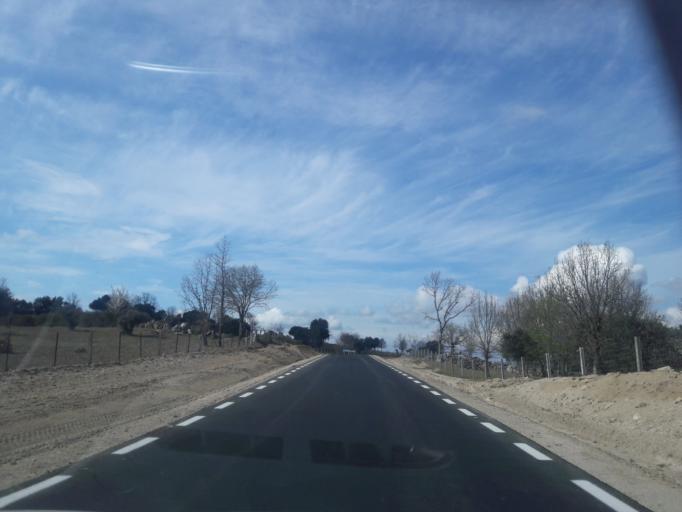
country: ES
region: Castille and Leon
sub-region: Provincia de Salamanca
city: Monleon
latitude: 40.5369
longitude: -5.8171
